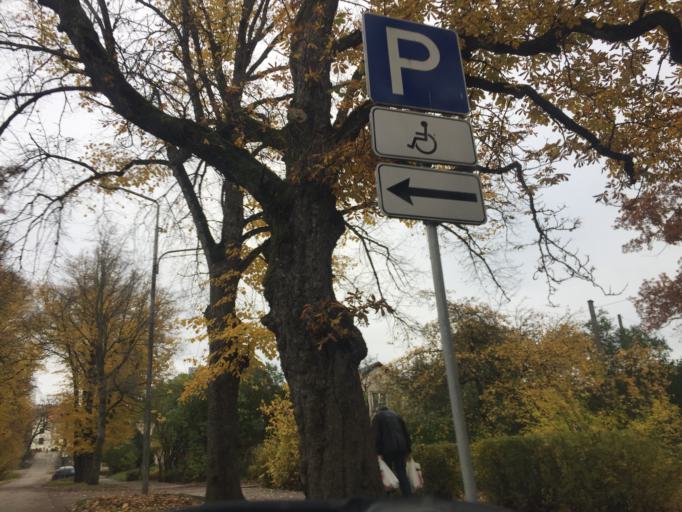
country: LV
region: Saldus Rajons
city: Saldus
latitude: 56.6666
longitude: 22.5103
